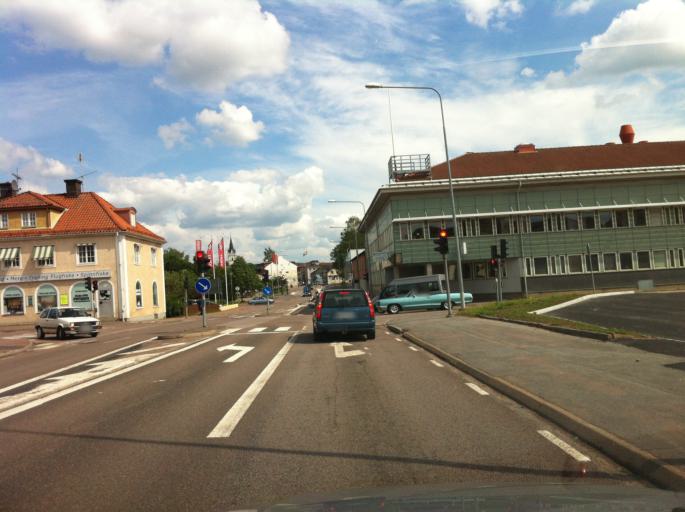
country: SE
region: Vaermland
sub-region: Sunne Kommun
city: Sunne
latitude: 59.8378
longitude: 13.1404
